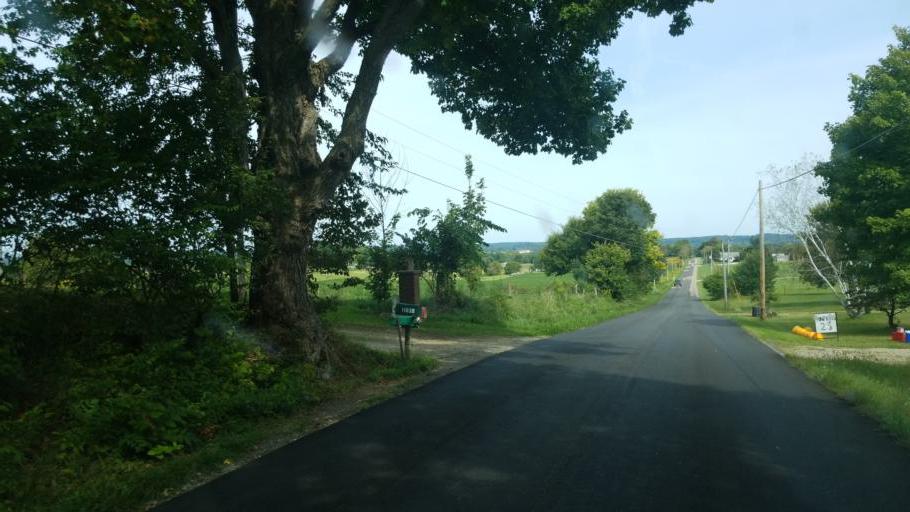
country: US
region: Ohio
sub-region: Knox County
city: Mount Vernon
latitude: 40.3839
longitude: -82.5329
